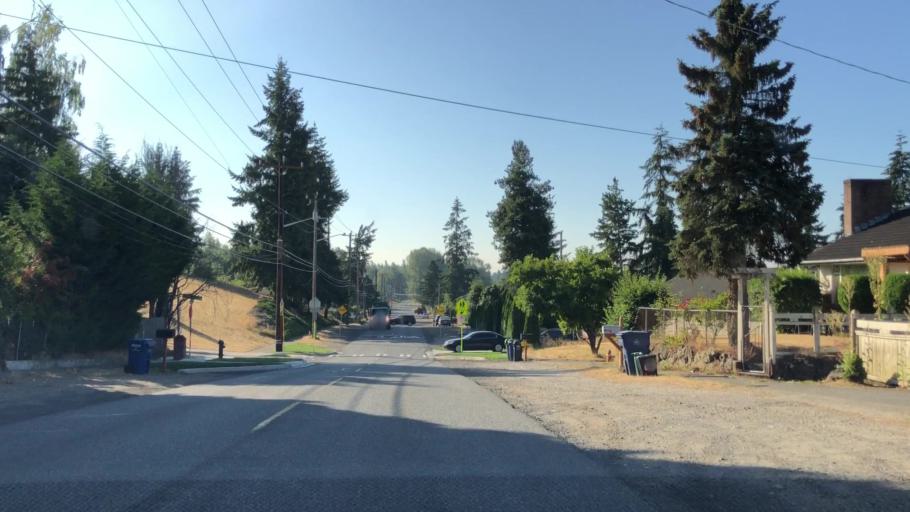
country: US
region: Washington
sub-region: King County
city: Bryn Mawr-Skyway
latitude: 47.4990
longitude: -122.2650
